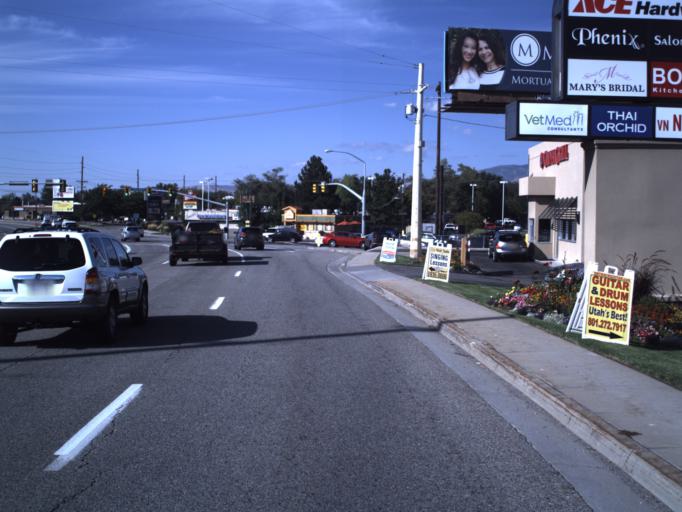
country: US
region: Utah
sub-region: Salt Lake County
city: Cottonwood Heights
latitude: 40.6376
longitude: -111.8341
